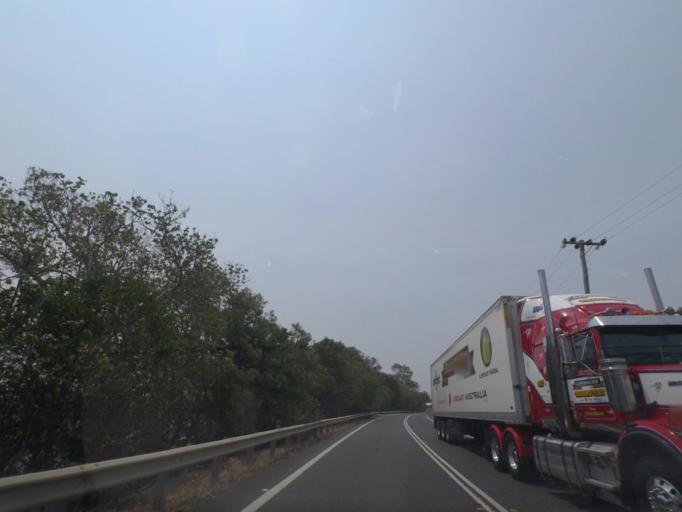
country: AU
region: New South Wales
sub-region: Richmond Valley
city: Evans Head
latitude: -28.9729
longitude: 153.4606
